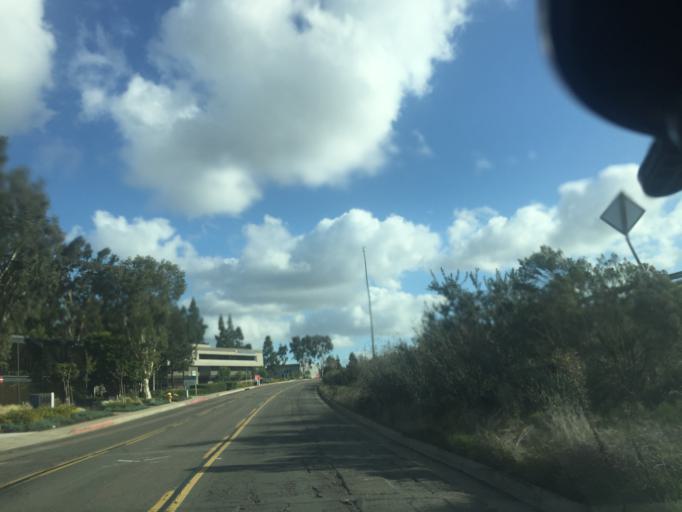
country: US
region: California
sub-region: San Diego County
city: San Diego
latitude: 32.7780
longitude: -117.1201
